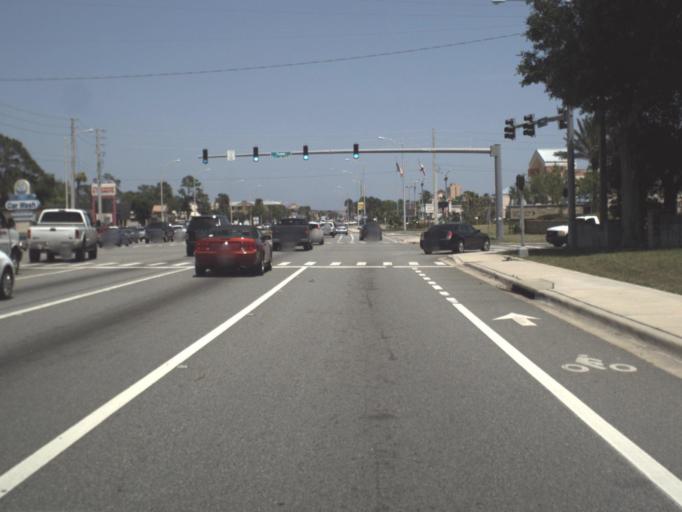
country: US
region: Florida
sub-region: Duval County
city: Jacksonville Beach
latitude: 30.2880
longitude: -81.4062
